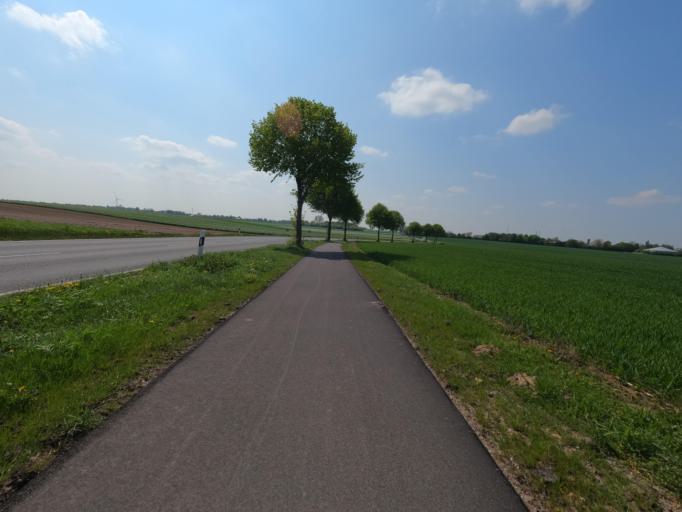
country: DE
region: North Rhine-Westphalia
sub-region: Regierungsbezirk Koln
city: Heinsberg
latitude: 51.0285
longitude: 6.1036
